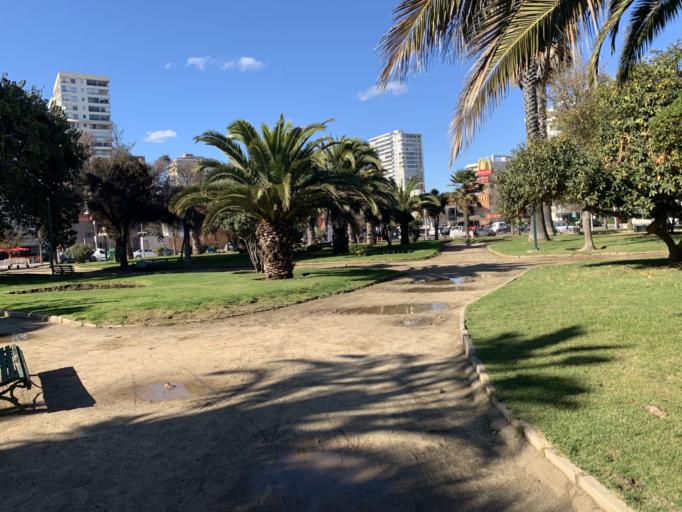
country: CL
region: Valparaiso
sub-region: Provincia de Valparaiso
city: Vina del Mar
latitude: -33.0176
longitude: -71.5593
